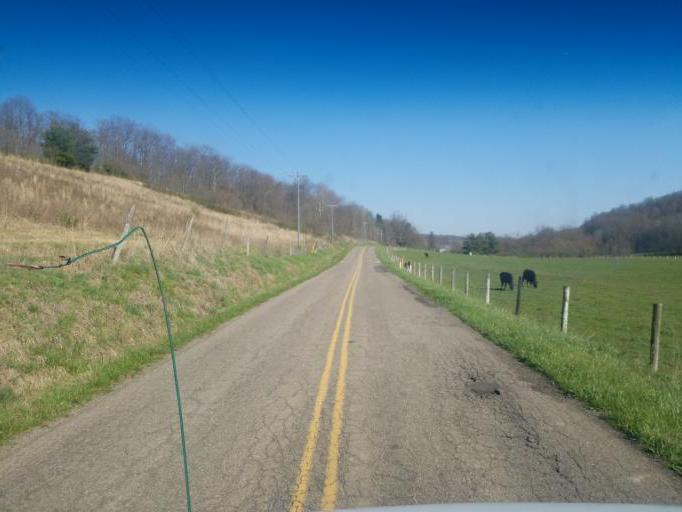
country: US
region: Ohio
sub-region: Knox County
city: Oak Hill
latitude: 40.2550
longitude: -82.2165
